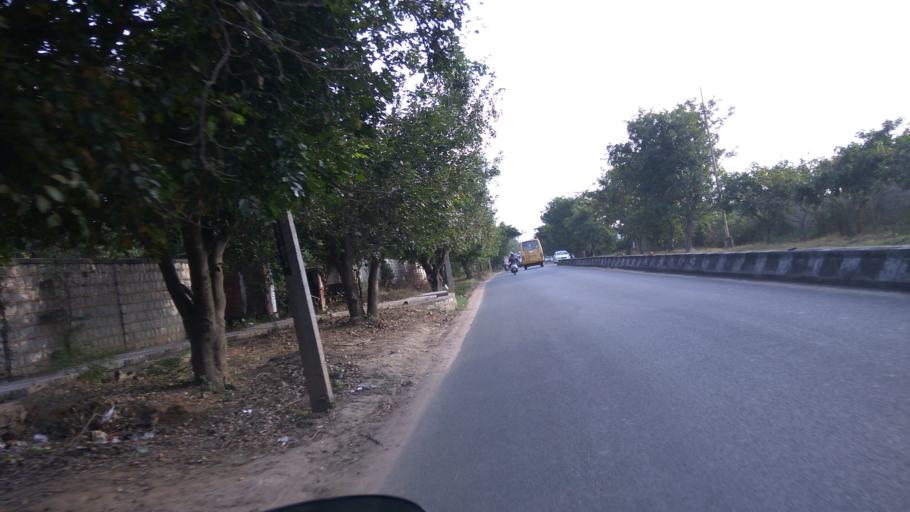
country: IN
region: Karnataka
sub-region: Bangalore Urban
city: Bangalore
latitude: 12.9610
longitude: 77.6908
